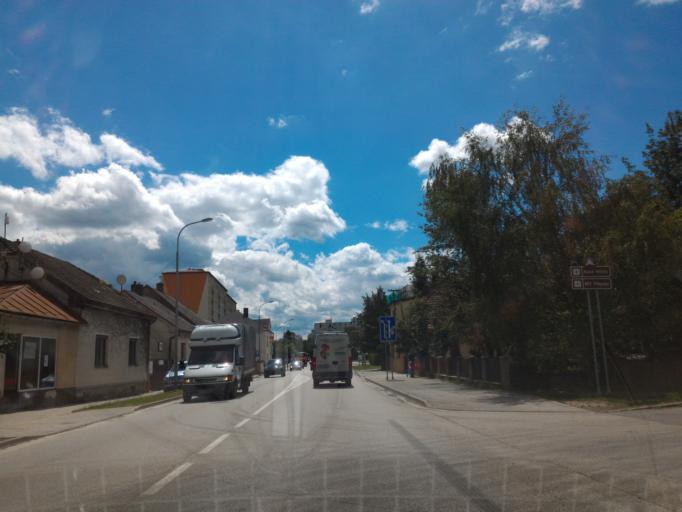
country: CZ
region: Vysocina
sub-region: Okres Zd'ar nad Sazavou
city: Zd'ar nad Sazavou
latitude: 49.5698
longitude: 15.9425
